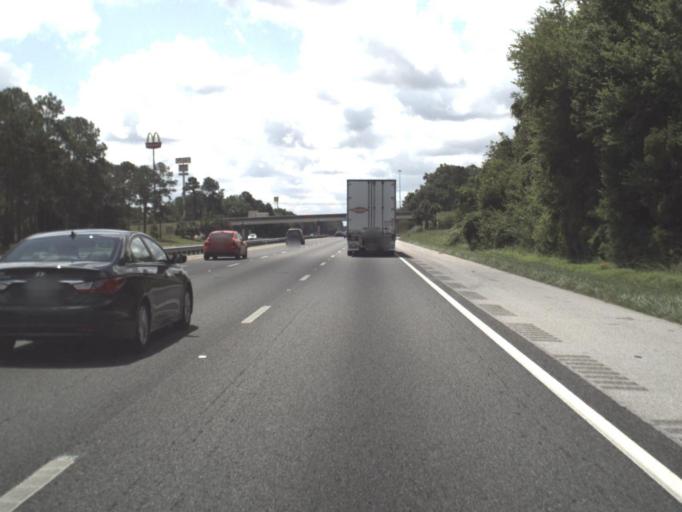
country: US
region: Florida
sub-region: Suwannee County
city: Wellborn
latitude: 30.3193
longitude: -82.8095
